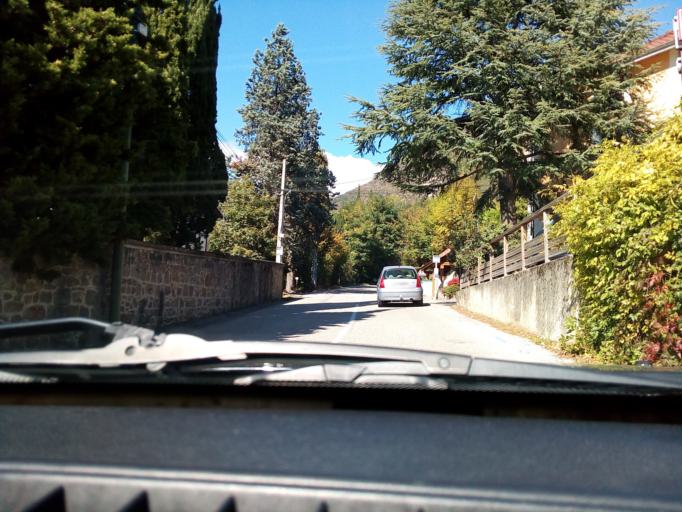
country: FR
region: Rhone-Alpes
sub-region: Departement de l'Isere
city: Corenc
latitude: 45.2179
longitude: 5.7606
